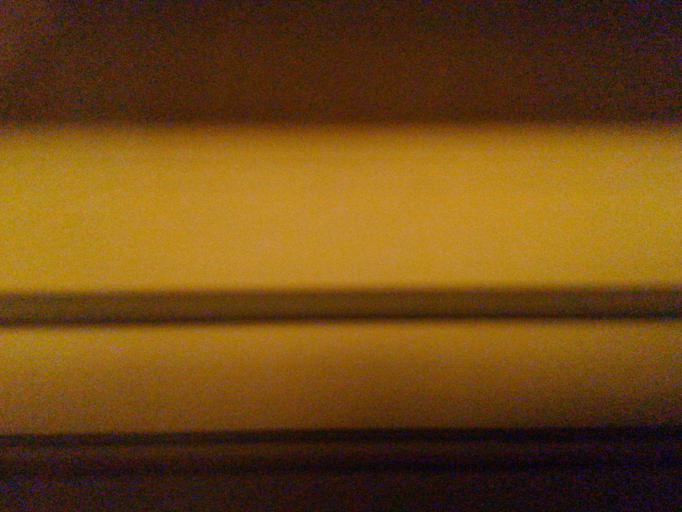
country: JP
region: Miyagi
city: Furukawa
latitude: 38.4962
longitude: 140.9589
